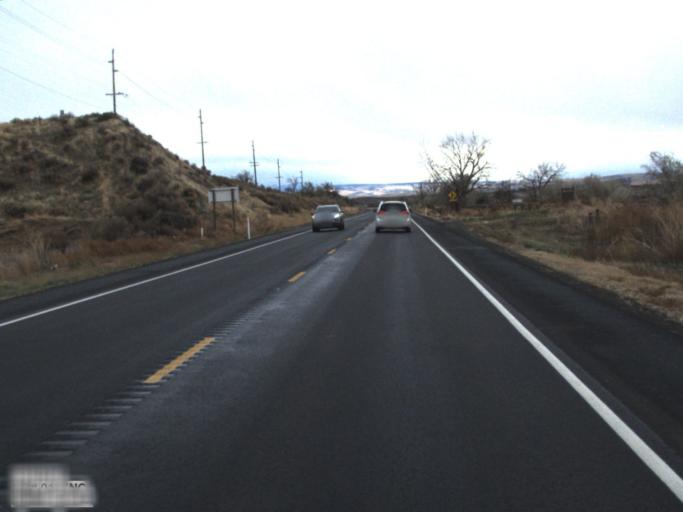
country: US
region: Washington
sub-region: Walla Walla County
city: Garrett
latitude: 46.0445
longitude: -118.6933
